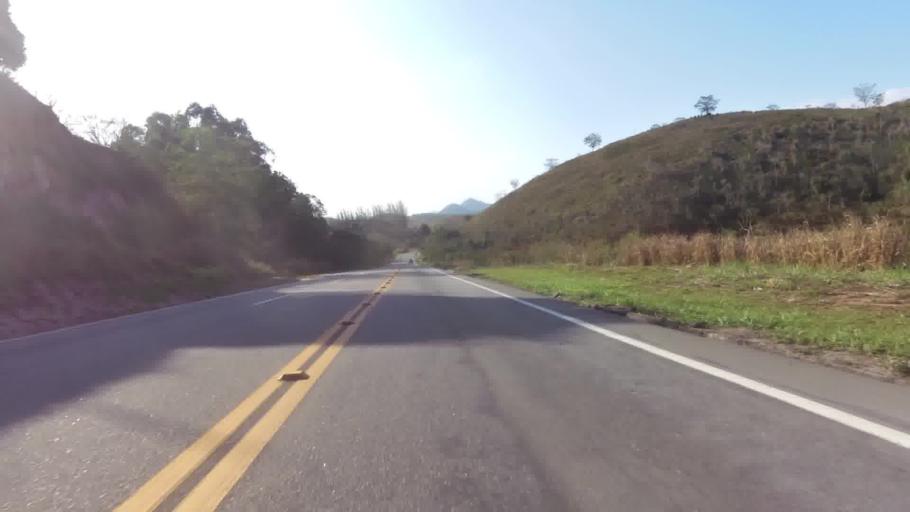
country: BR
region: Espirito Santo
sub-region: Mimoso Do Sul
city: Mimoso do Sul
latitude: -21.2052
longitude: -41.2995
